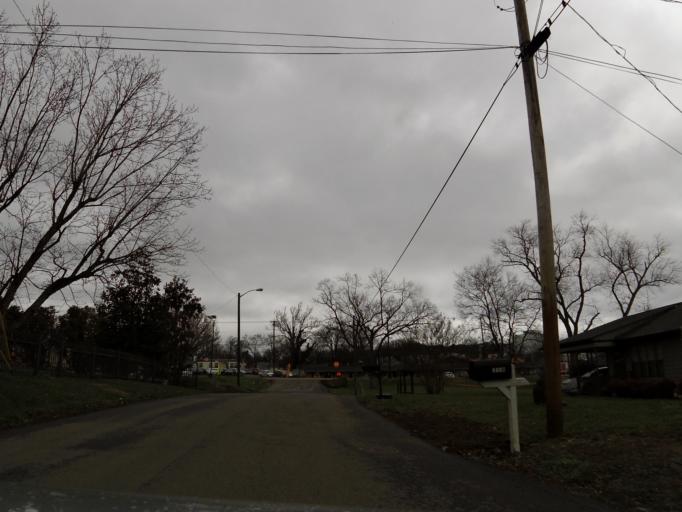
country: US
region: Tennessee
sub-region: Knox County
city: Knoxville
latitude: 35.9738
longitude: -83.9727
